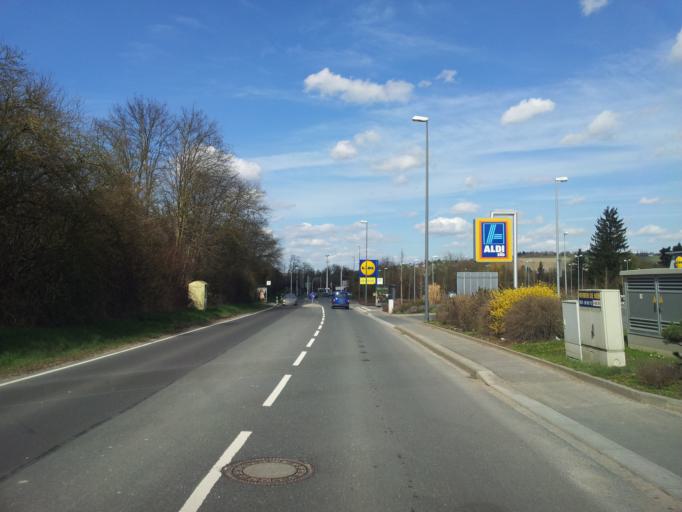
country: DE
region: Bavaria
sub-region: Regierungsbezirk Unterfranken
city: Reichenberg
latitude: 49.7561
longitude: 9.9426
